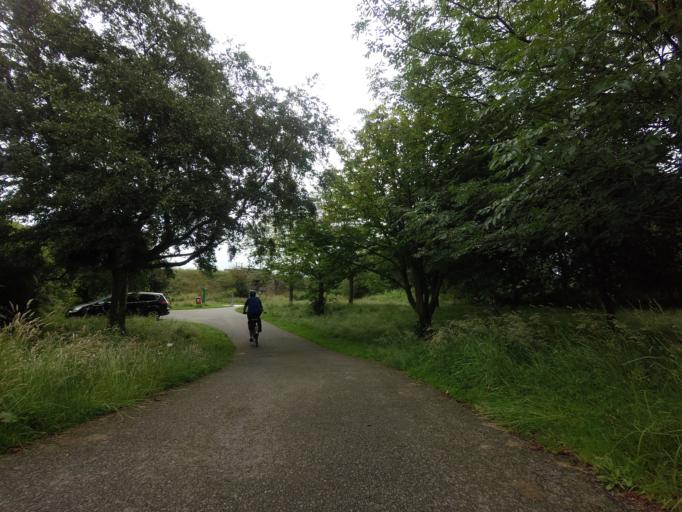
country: GB
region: Scotland
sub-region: Moray
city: Fochabers
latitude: 57.6622
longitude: -3.1132
